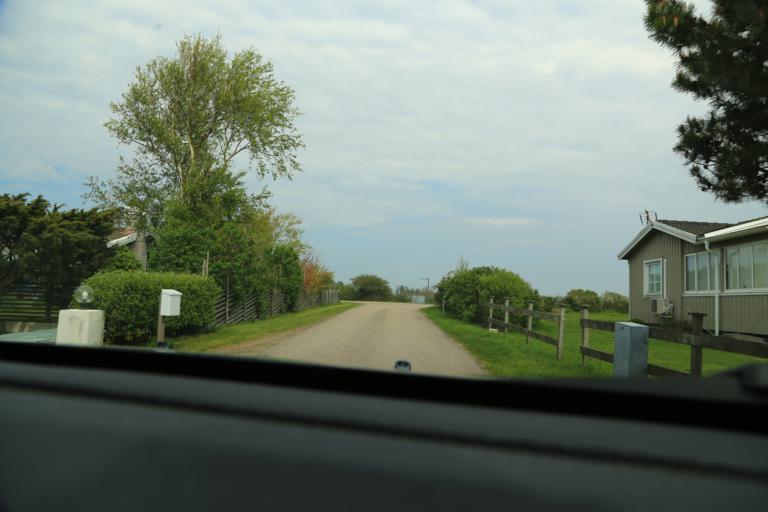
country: SE
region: Halland
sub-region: Varbergs Kommun
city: Varberg
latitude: 57.1417
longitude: 12.2230
